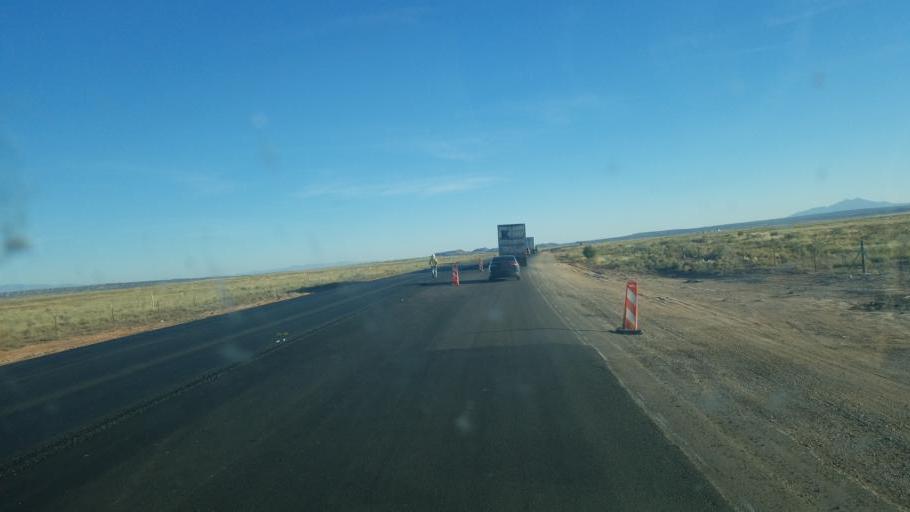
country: US
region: New Mexico
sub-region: Valencia County
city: Los Lunas
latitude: 34.8745
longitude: -107.0554
